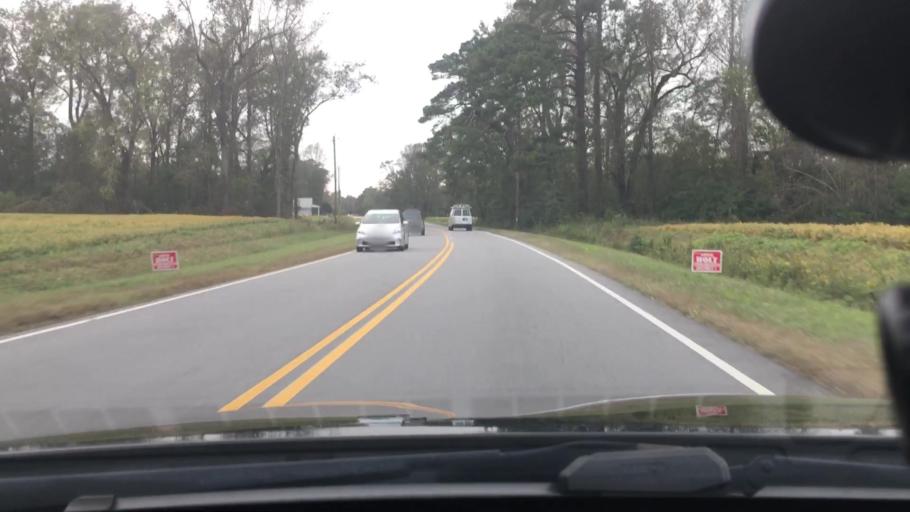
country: US
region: North Carolina
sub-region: Craven County
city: Vanceboro
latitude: 35.2915
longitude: -77.1334
